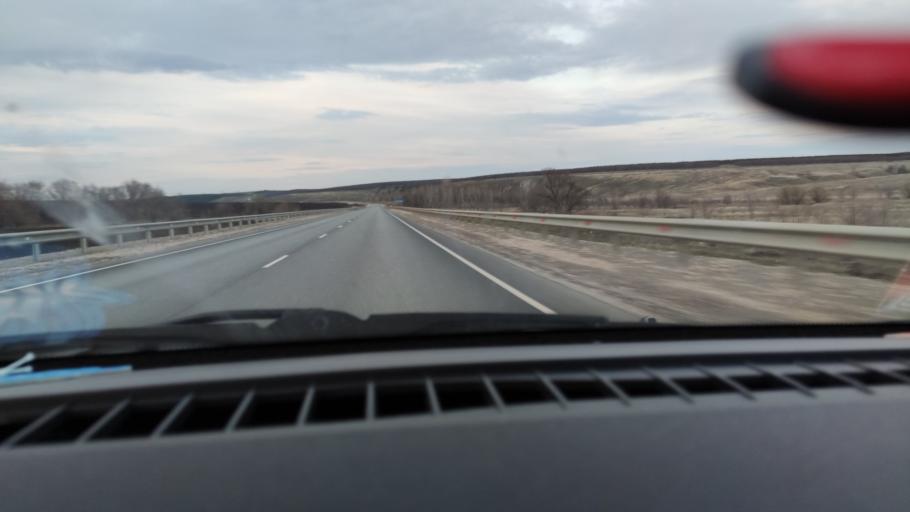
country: RU
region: Saratov
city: Yelshanka
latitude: 51.8551
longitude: 46.4935
